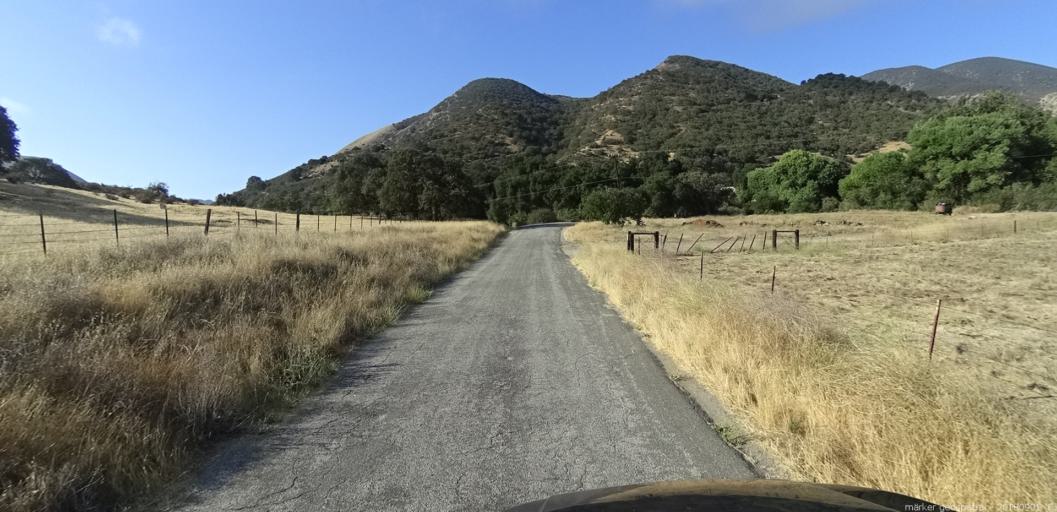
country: US
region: California
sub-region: Monterey County
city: Greenfield
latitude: 36.2416
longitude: -121.2868
